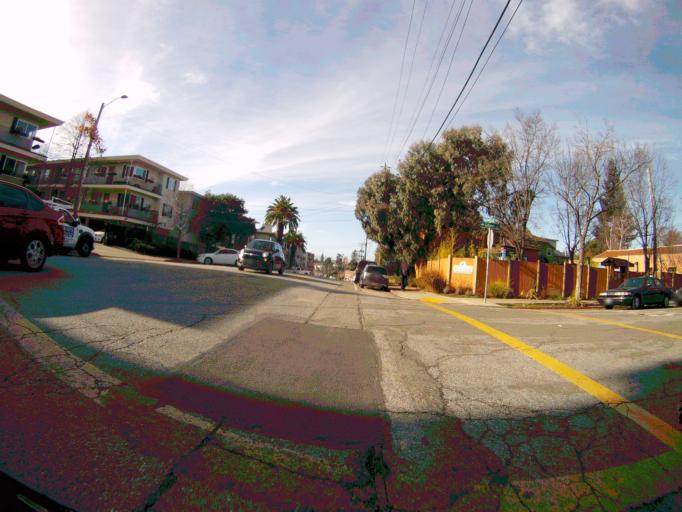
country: US
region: California
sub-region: Alameda County
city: Piedmont
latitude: 37.8279
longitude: -122.2546
